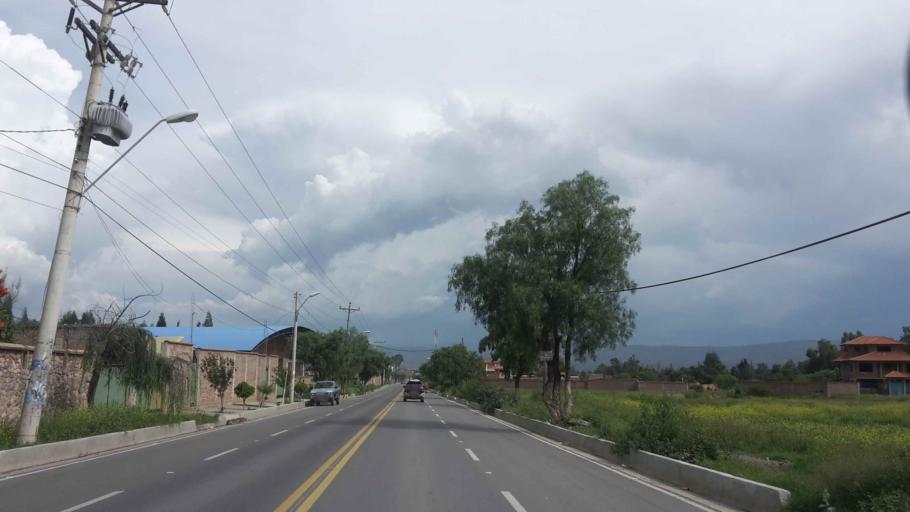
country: BO
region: Cochabamba
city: Cochabamba
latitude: -17.3441
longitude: -66.2601
